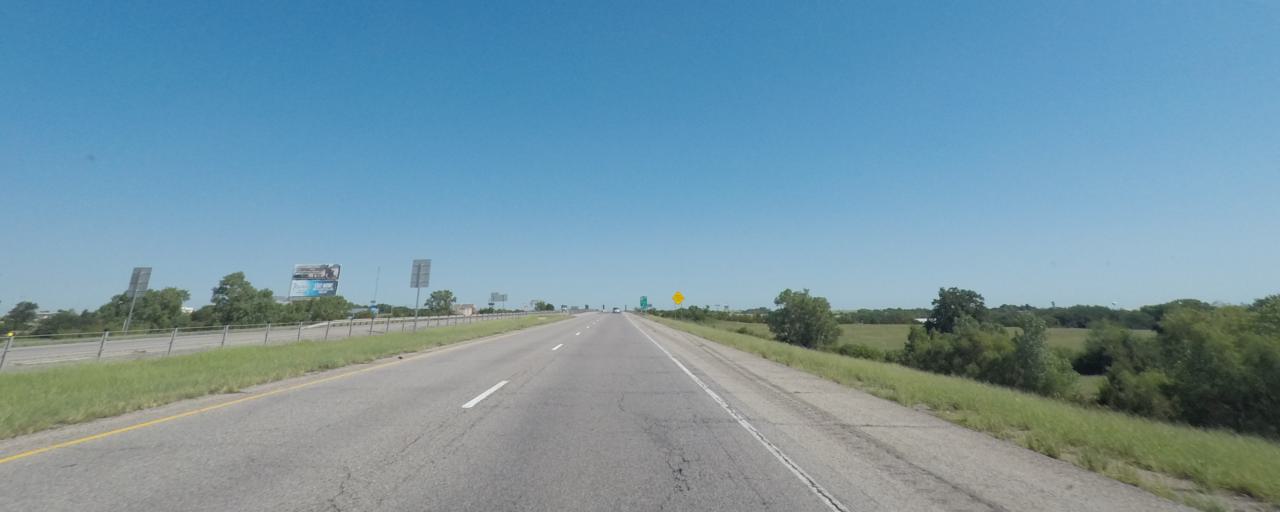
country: US
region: Oklahoma
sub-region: Noble County
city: Perry
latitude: 36.2819
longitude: -97.3276
